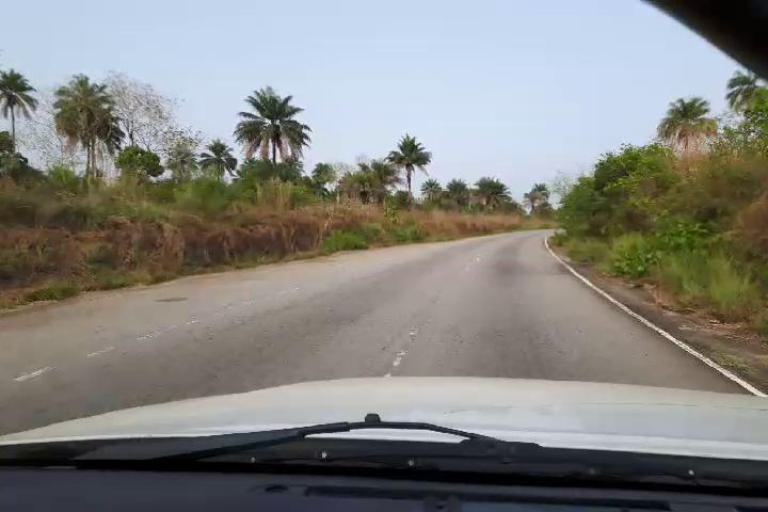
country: SL
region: Eastern Province
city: Blama
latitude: 7.9401
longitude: -11.5001
